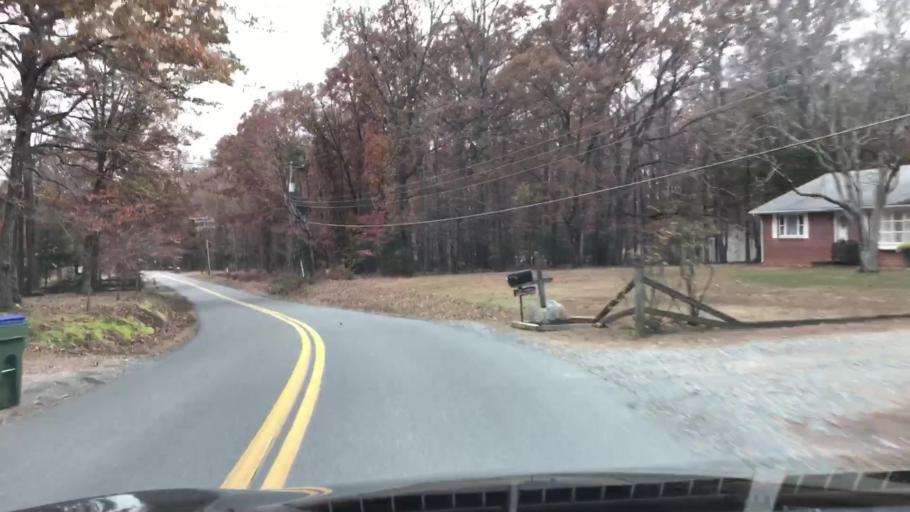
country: US
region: Virginia
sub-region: Stafford County
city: Falmouth
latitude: 38.3993
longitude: -77.5761
